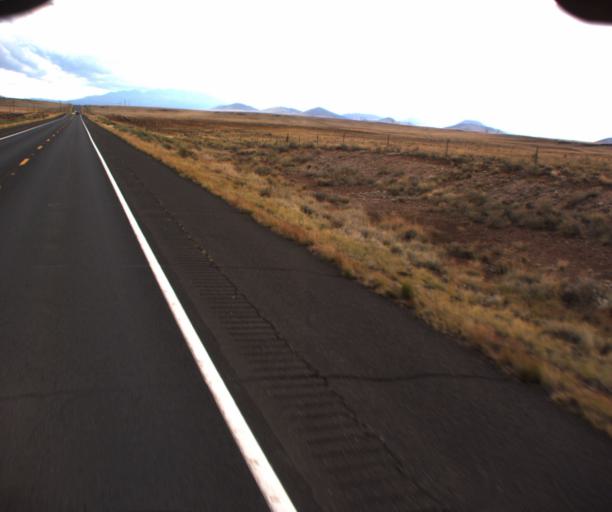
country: US
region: Arizona
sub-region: Coconino County
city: Flagstaff
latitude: 35.6696
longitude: -111.5105
